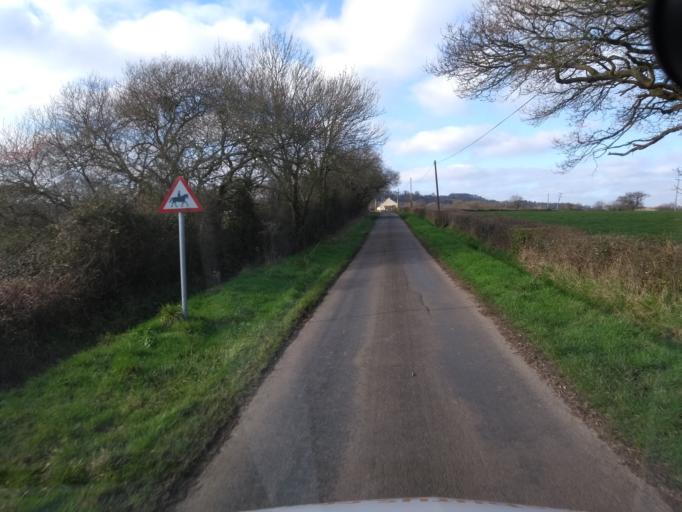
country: GB
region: England
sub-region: Somerset
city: Chard
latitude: 50.9338
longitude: -3.0025
